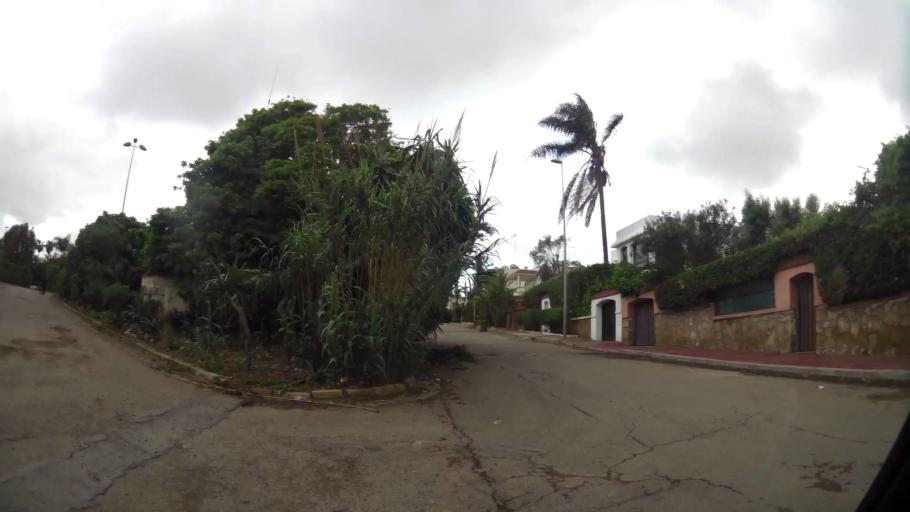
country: MA
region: Grand Casablanca
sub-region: Casablanca
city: Casablanca
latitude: 33.5847
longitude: -7.6805
